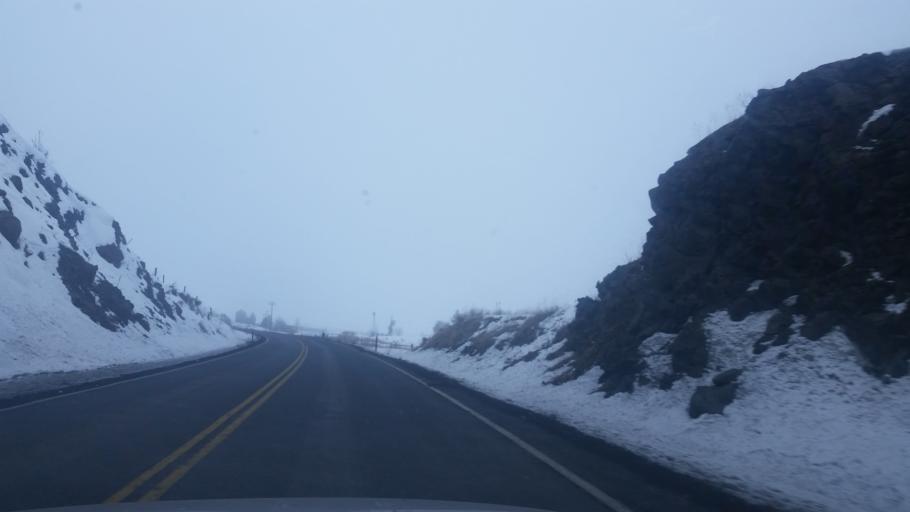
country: US
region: Washington
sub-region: Spokane County
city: Medical Lake
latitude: 47.7215
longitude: -117.8710
